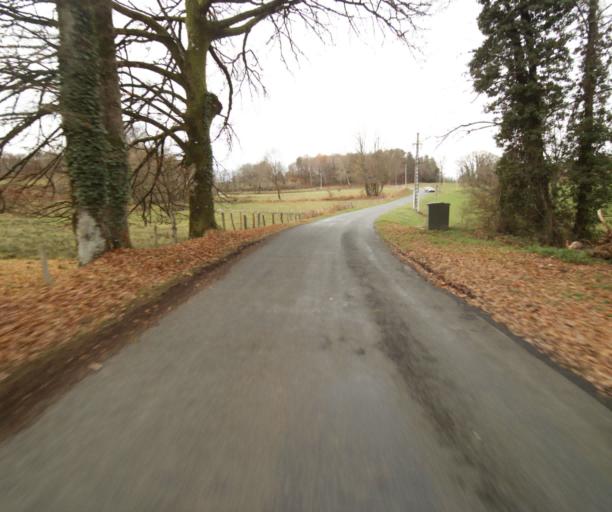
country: FR
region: Limousin
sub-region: Departement de la Correze
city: Chameyrat
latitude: 45.2499
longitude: 1.6827
